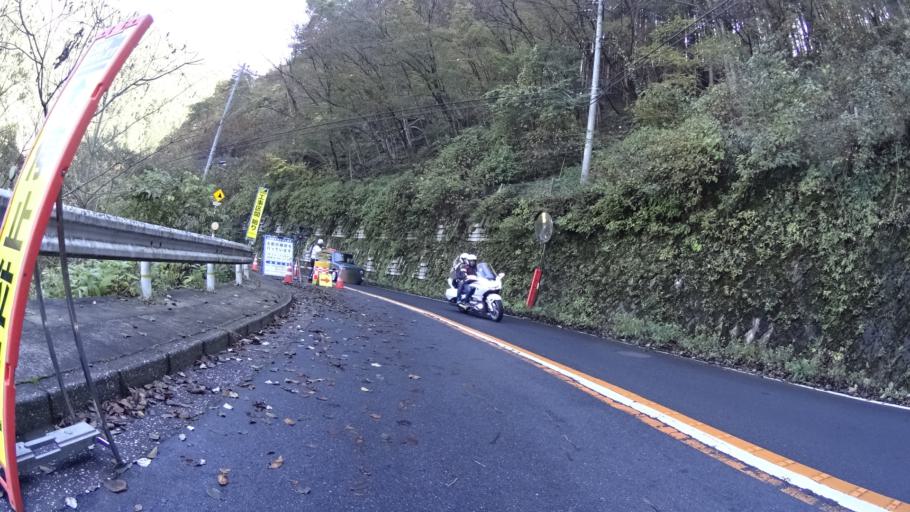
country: JP
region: Yamanashi
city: Uenohara
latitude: 35.7169
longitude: 139.0721
